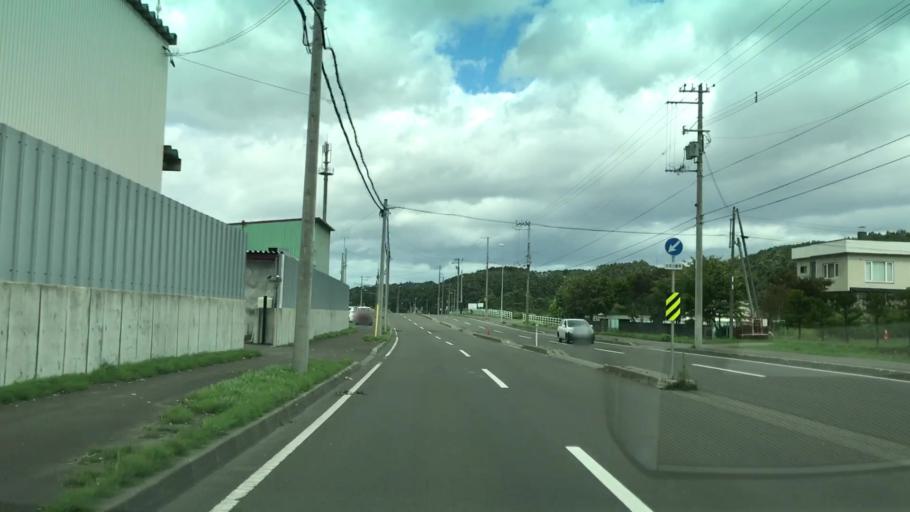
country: JP
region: Hokkaido
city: Kitahiroshima
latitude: 42.9723
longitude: 141.4511
